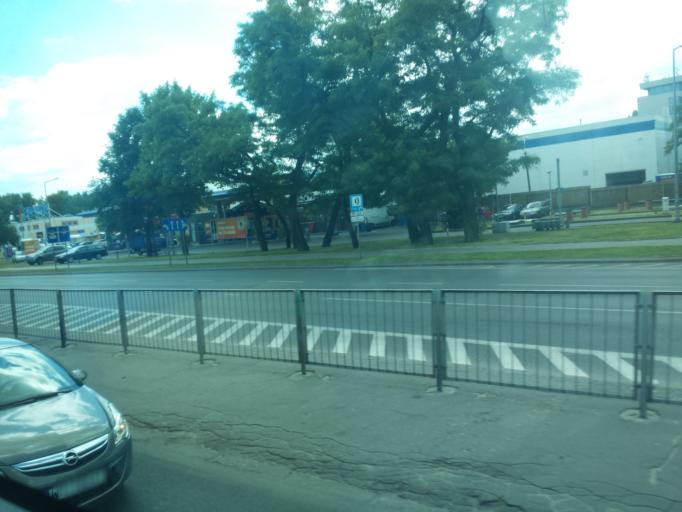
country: PL
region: Masovian Voivodeship
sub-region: Warszawa
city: Praga Poludnie
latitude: 52.2380
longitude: 21.1186
